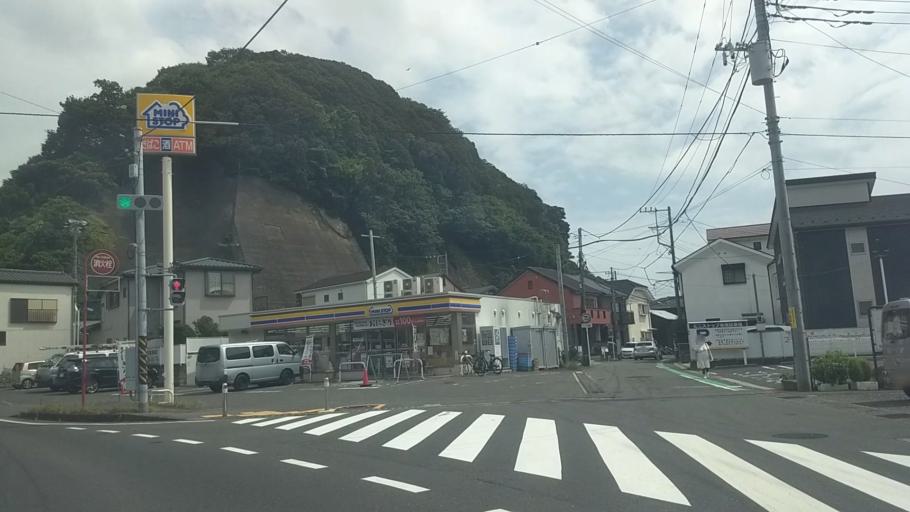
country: JP
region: Kanagawa
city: Yokosuka
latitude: 35.2449
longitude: 139.7212
